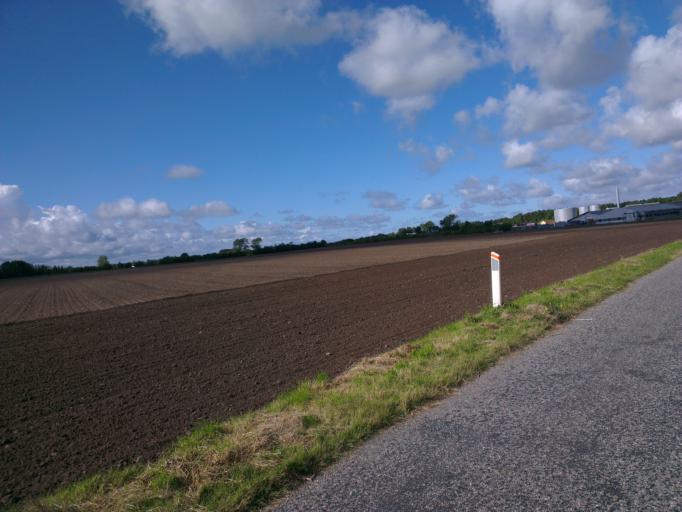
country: DK
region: Capital Region
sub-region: Frederikssund Kommune
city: Jaegerspris
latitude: 55.8272
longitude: 12.0006
